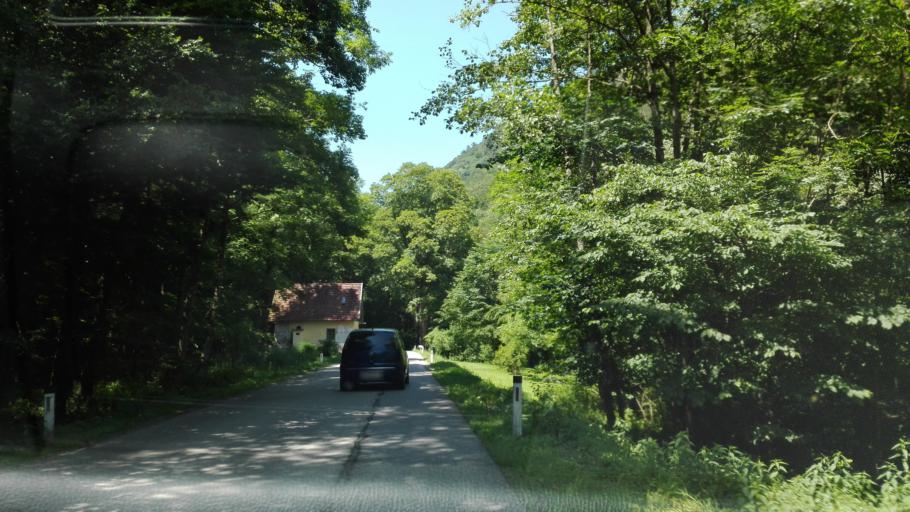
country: AT
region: Upper Austria
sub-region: Politischer Bezirk Rohrbach
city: Kleinzell im Muehlkreis
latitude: 48.3785
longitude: 13.9336
